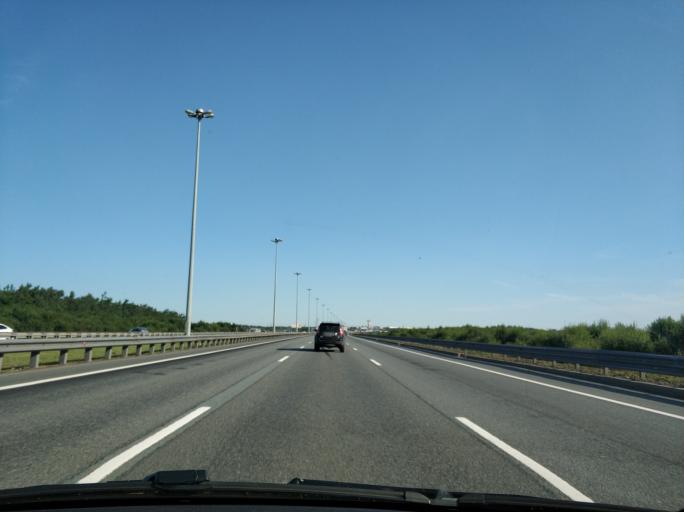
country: RU
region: Leningrad
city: Bugry
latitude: 60.0715
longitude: 30.3827
